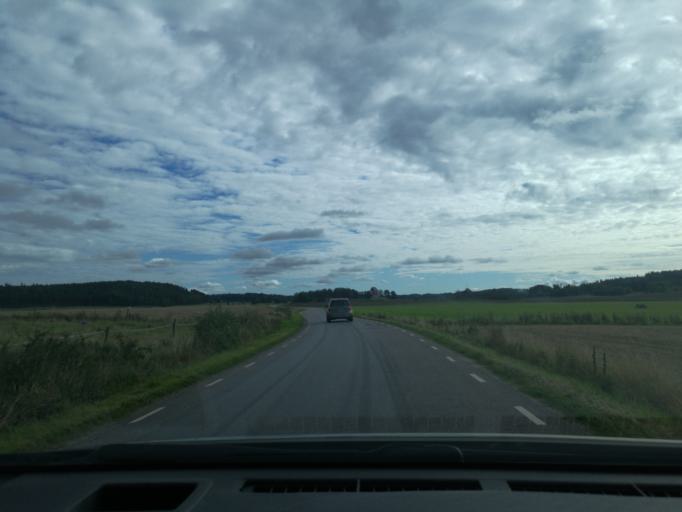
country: SE
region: OEstergoetland
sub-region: Soderkopings Kommun
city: Soederkoeping
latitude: 58.5042
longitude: 16.4616
